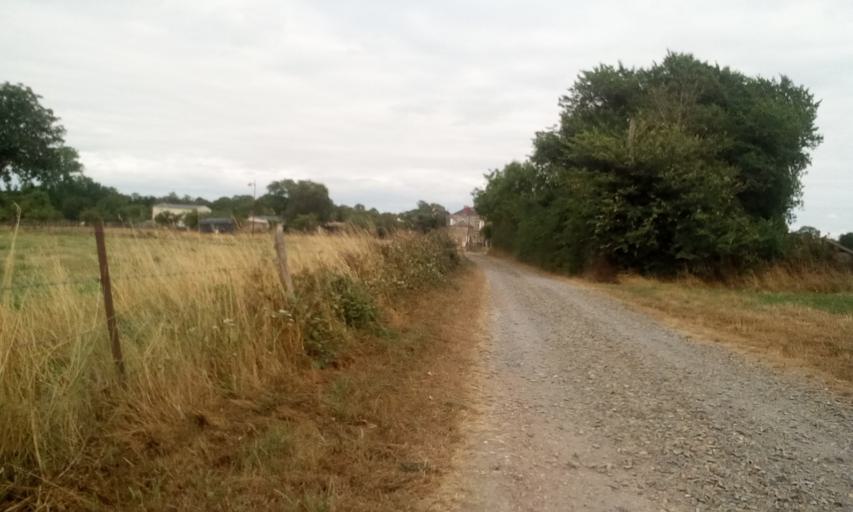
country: FR
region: Lower Normandy
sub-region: Departement du Calvados
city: Thury-Harcourt
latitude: 48.9781
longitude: -0.4268
